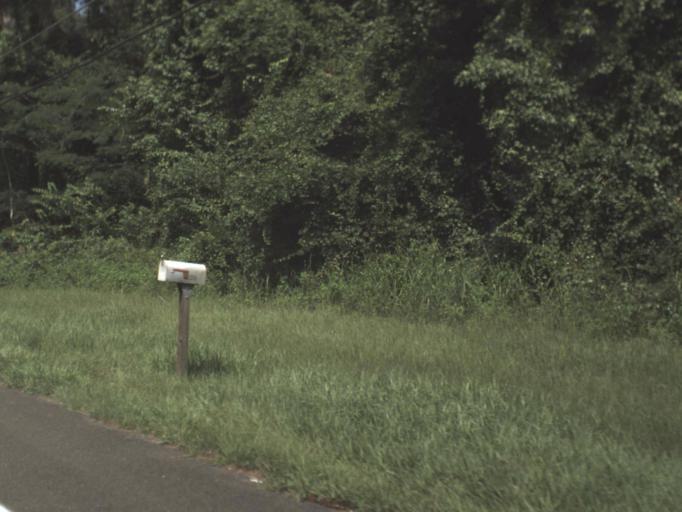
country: US
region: Florida
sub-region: Alachua County
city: Gainesville
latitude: 29.6741
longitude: -82.2403
